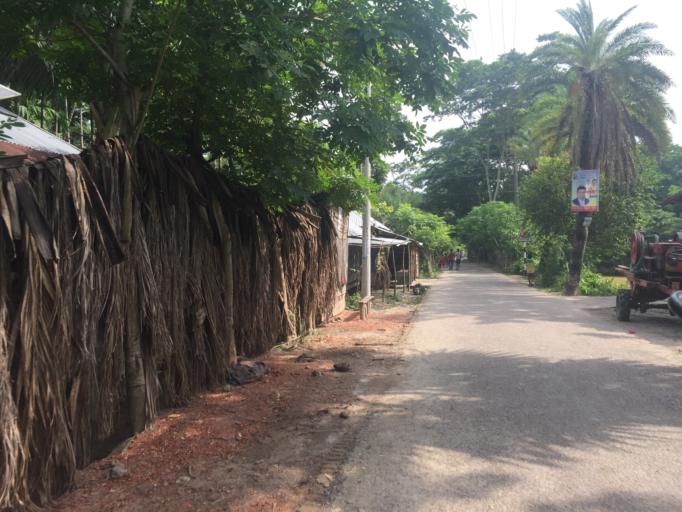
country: BD
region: Barisal
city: Mathba
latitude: 22.2606
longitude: 89.9116
